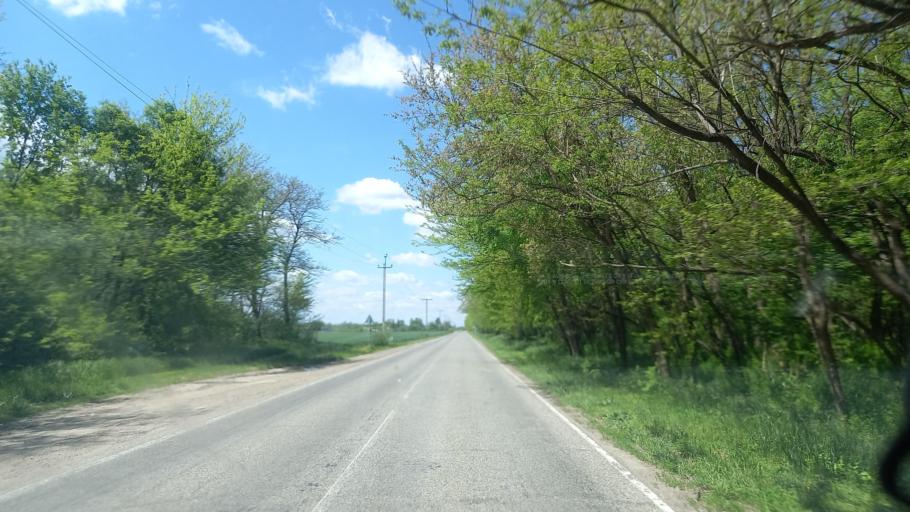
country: RU
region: Krasnodarskiy
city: Tbilisskaya
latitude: 45.3377
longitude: 40.3103
